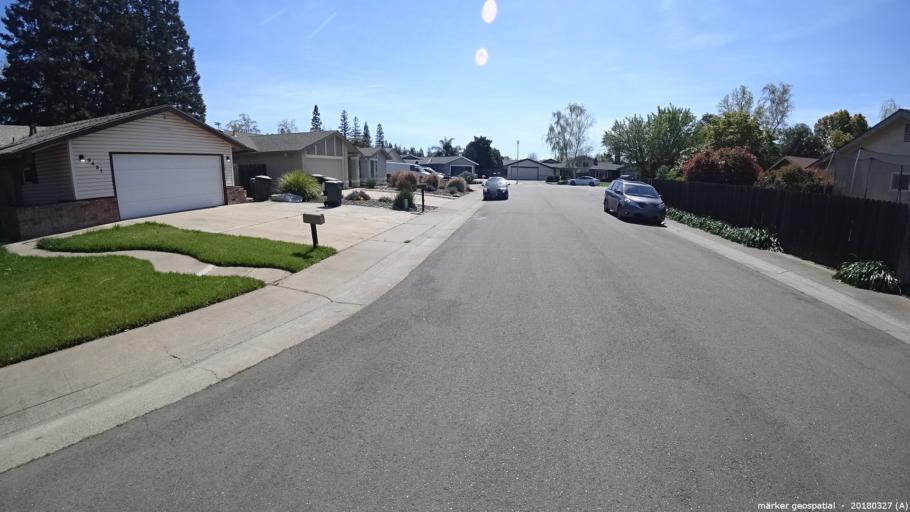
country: US
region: California
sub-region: Sacramento County
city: La Riviera
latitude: 38.5562
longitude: -121.3475
